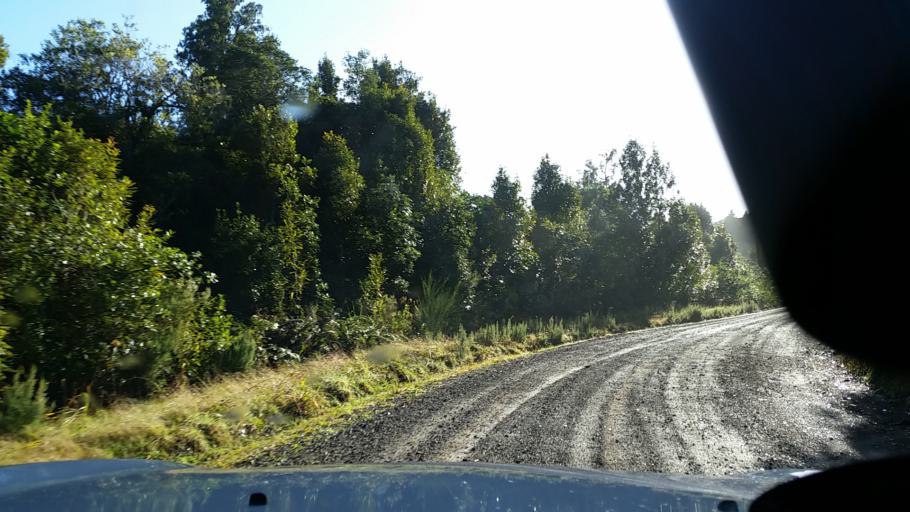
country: NZ
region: Bay of Plenty
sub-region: Kawerau District
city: Kawerau
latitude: -38.0036
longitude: 176.5970
